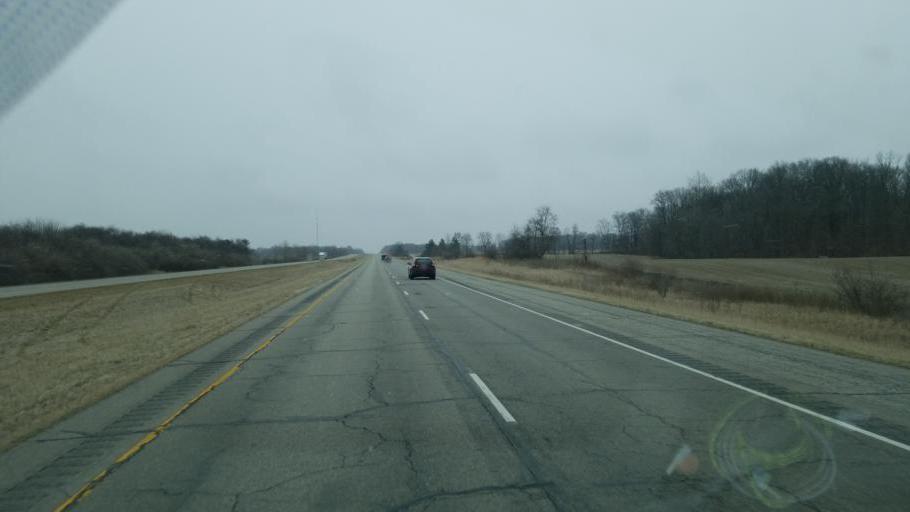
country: US
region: Indiana
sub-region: Wabash County
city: Wabash
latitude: 40.8073
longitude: -85.9370
